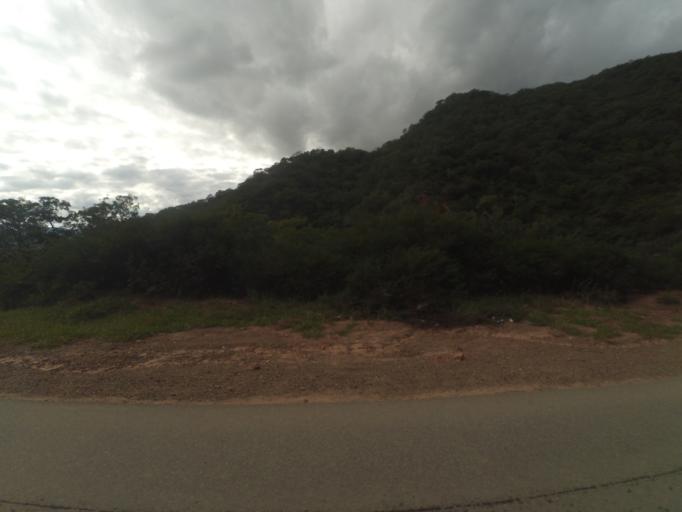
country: BO
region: Santa Cruz
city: Samaipata
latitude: -18.1659
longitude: -63.9007
